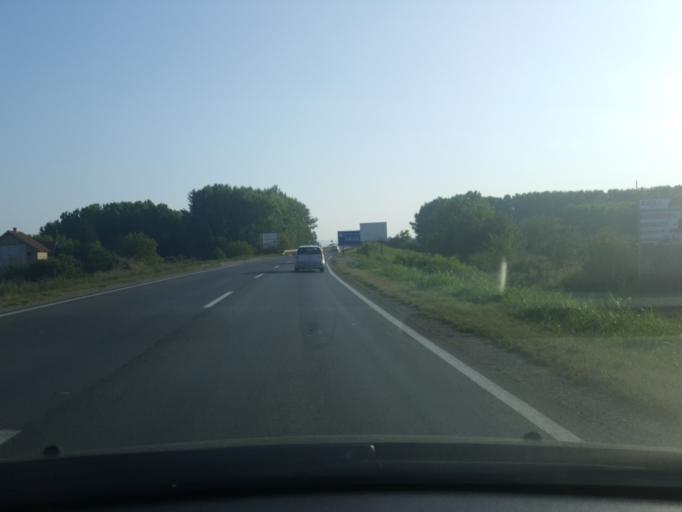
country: RS
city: Klenak
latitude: 44.7624
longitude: 19.7225
